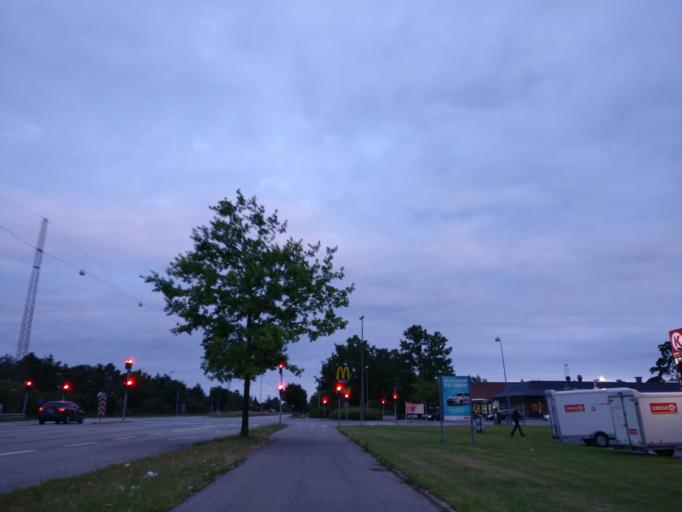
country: DK
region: Capital Region
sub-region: Hvidovre Kommune
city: Hvidovre
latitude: 55.6459
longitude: 12.4605
